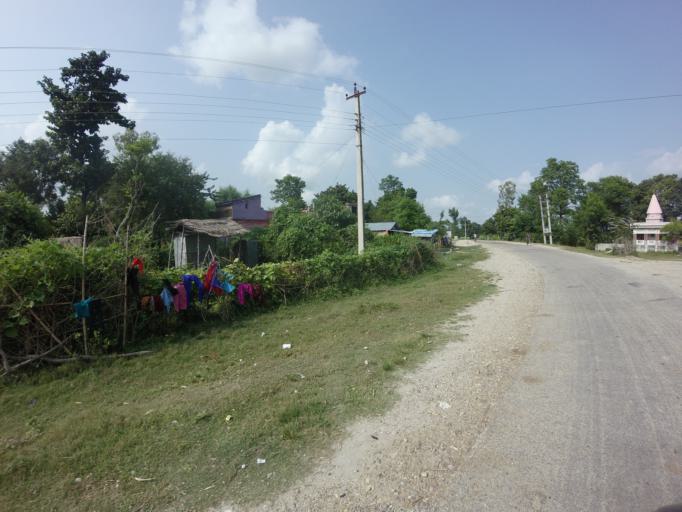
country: NP
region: Far Western
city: Tikapur
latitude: 28.4562
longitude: 81.0763
